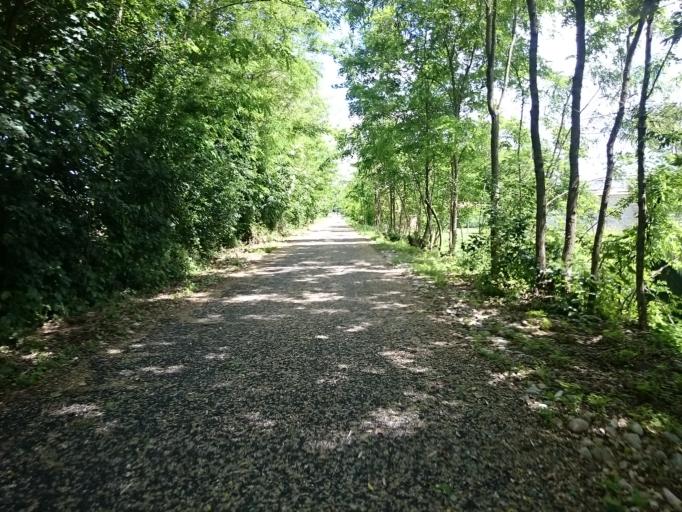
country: IT
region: Veneto
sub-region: Provincia di Padova
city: Campodoro
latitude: 45.5006
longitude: 11.7419
